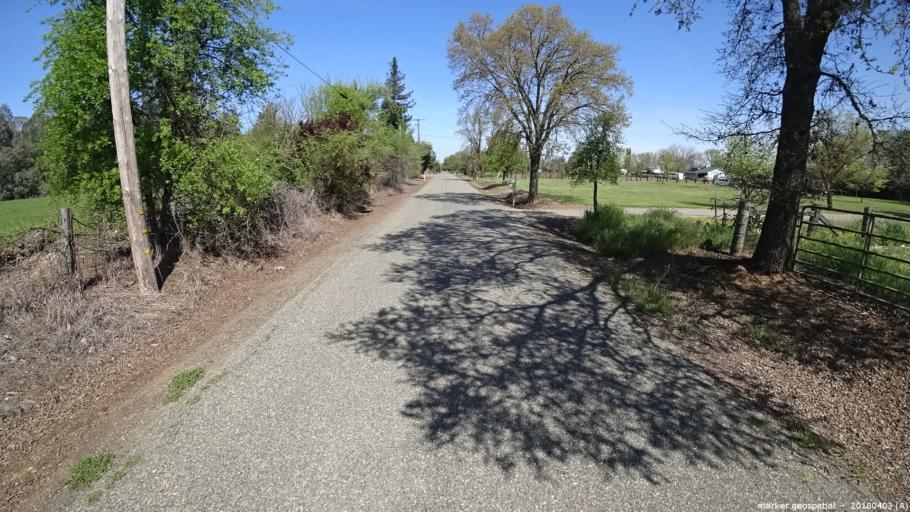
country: US
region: California
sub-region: Sacramento County
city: Wilton
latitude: 38.3974
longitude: -121.2875
